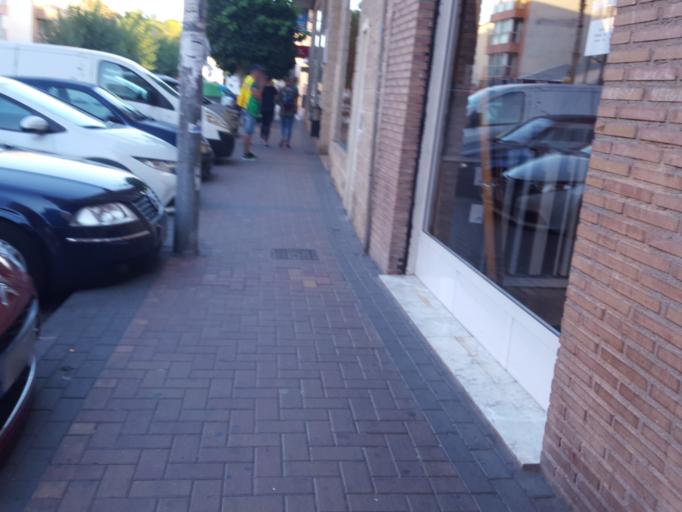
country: ES
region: Murcia
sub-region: Murcia
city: Murcia
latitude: 38.0083
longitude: -1.1516
